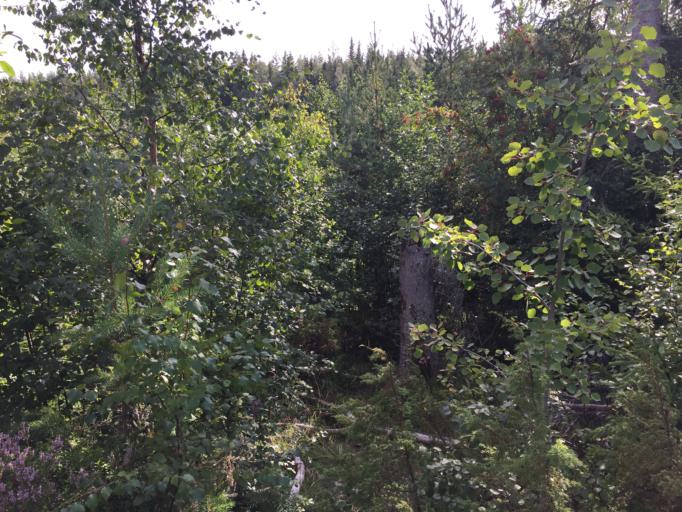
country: SE
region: Gaevleborg
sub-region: Ljusdals Kommun
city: Ljusdal
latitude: 61.8230
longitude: 16.0016
